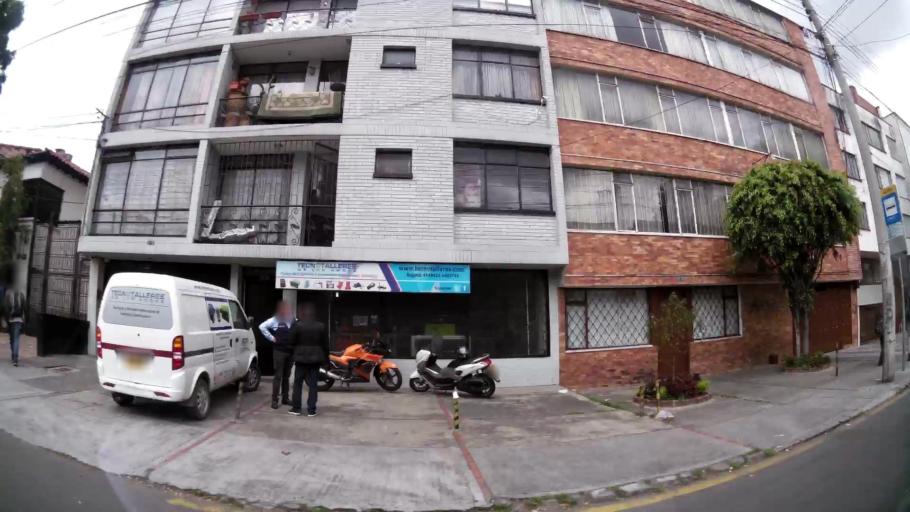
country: CO
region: Bogota D.C.
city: Bogota
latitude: 4.6269
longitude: -74.0731
